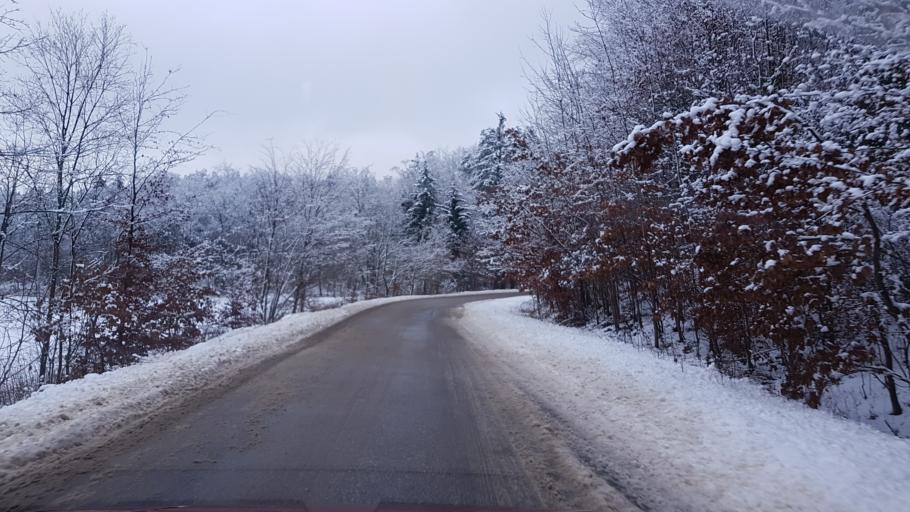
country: PL
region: West Pomeranian Voivodeship
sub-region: Powiat drawski
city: Zlocieniec
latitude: 53.5039
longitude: 15.9988
